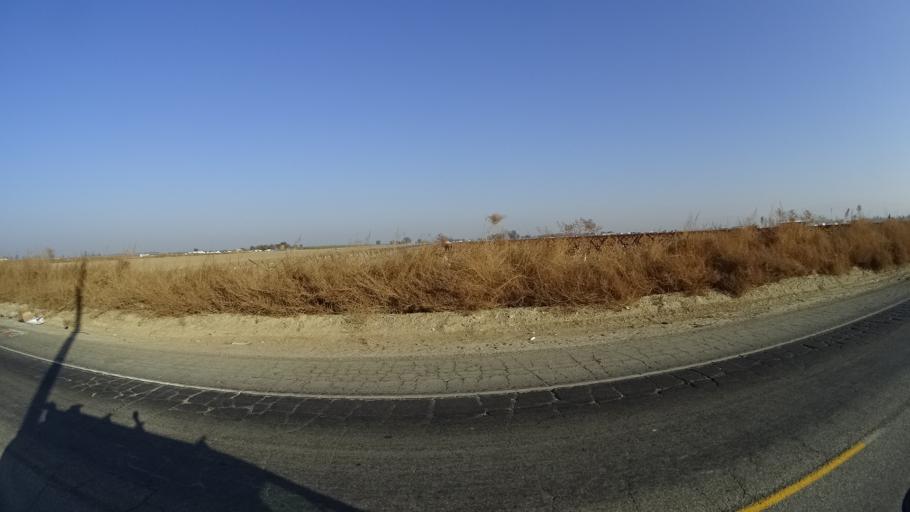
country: US
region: California
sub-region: Kern County
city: Greenfield
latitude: 35.2377
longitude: -118.9832
